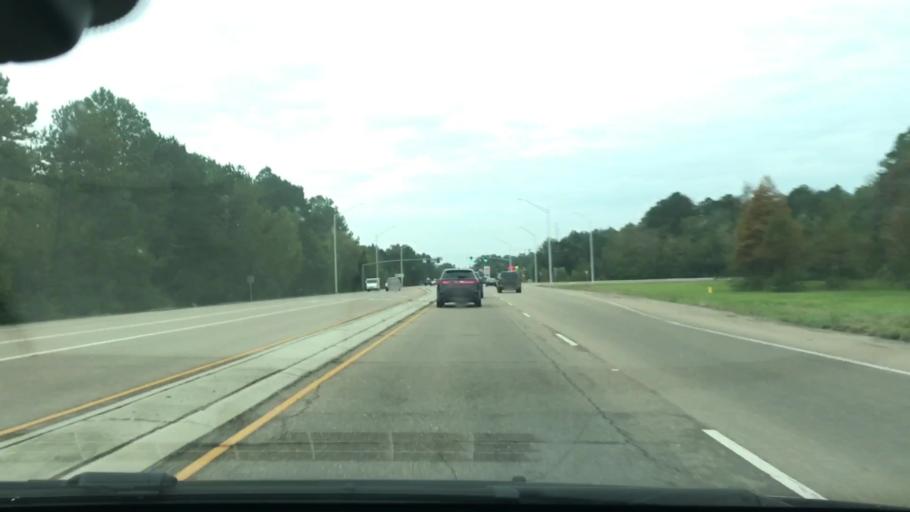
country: US
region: Louisiana
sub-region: Saint Tammany Parish
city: Slidell
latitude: 30.3099
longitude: -89.7709
